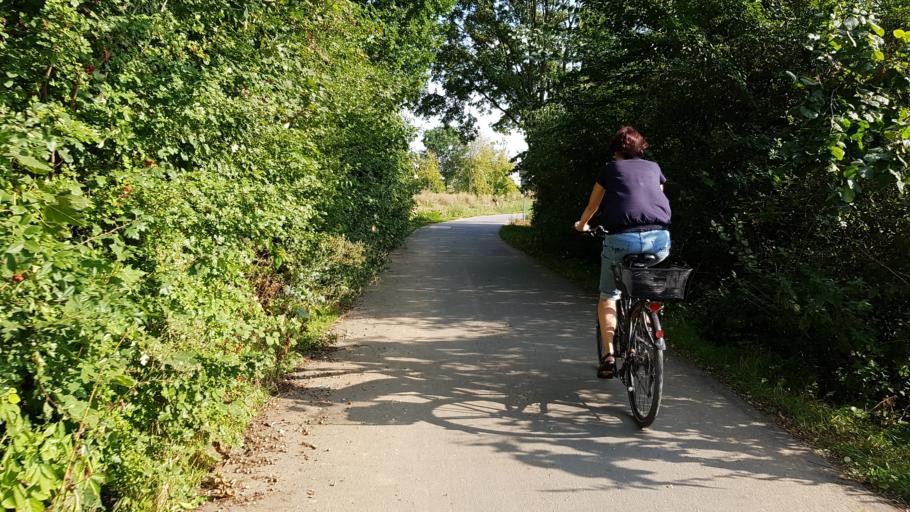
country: DE
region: Hesse
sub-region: Regierungsbezirk Darmstadt
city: Karben
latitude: 50.2361
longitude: 8.7636
